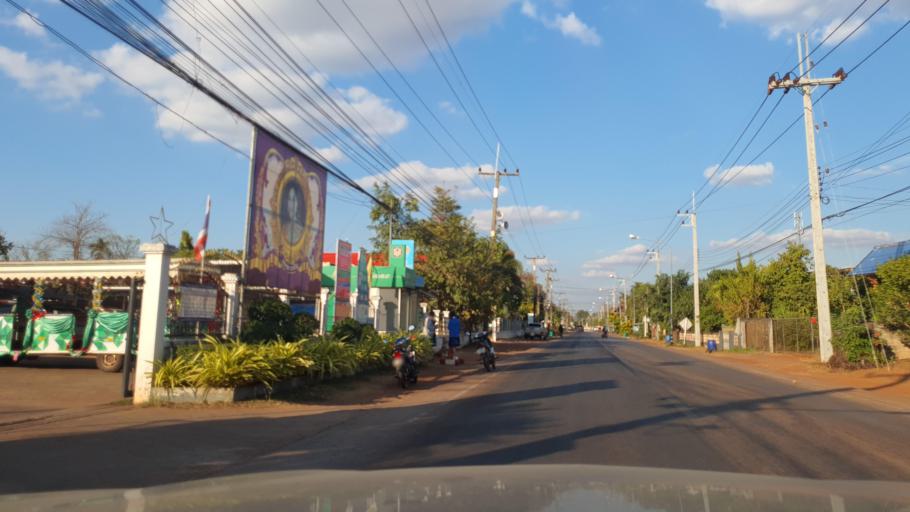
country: TH
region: Sakon Nakhon
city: Sakon Nakhon
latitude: 17.2584
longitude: 104.1887
